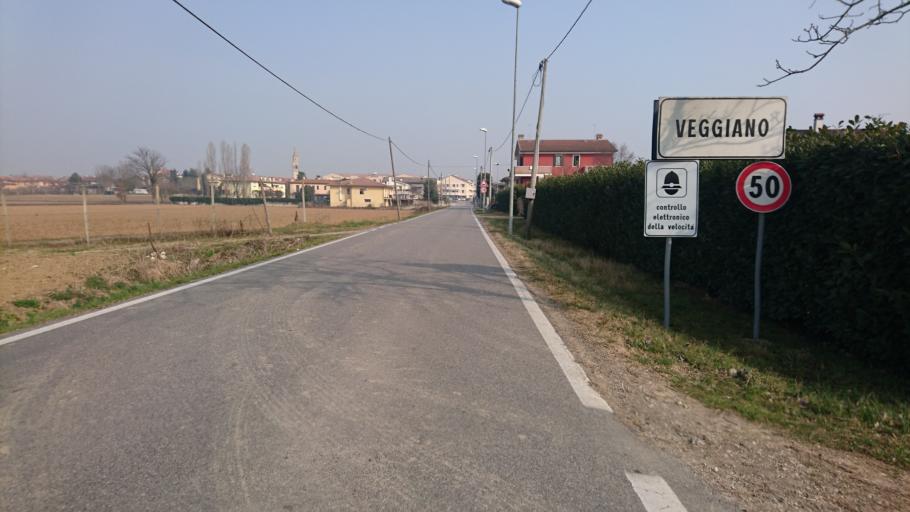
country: IT
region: Veneto
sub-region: Provincia di Padova
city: Veggiano
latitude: 45.4434
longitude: 11.7160
